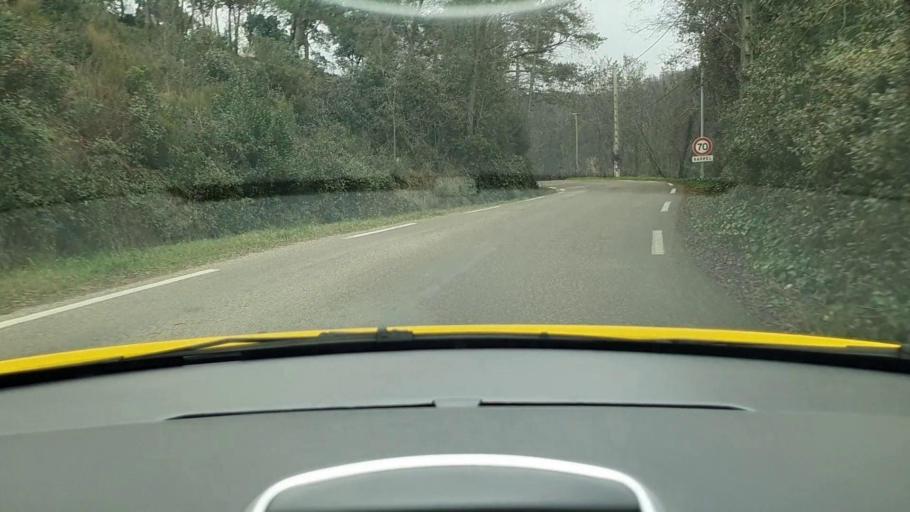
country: FR
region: Languedoc-Roussillon
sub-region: Departement du Gard
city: Besseges
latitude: 44.3110
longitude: 4.0904
